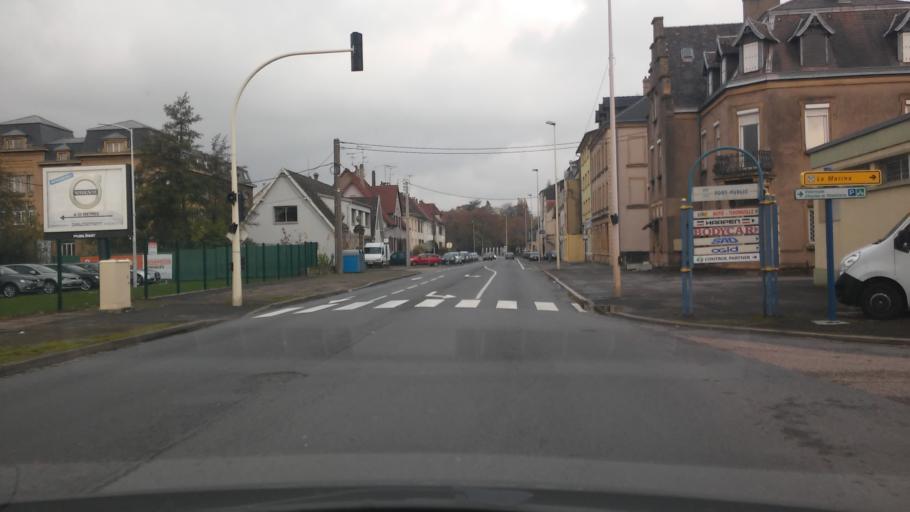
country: FR
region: Lorraine
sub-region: Departement de la Moselle
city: Terville
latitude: 49.3424
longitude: 6.1609
